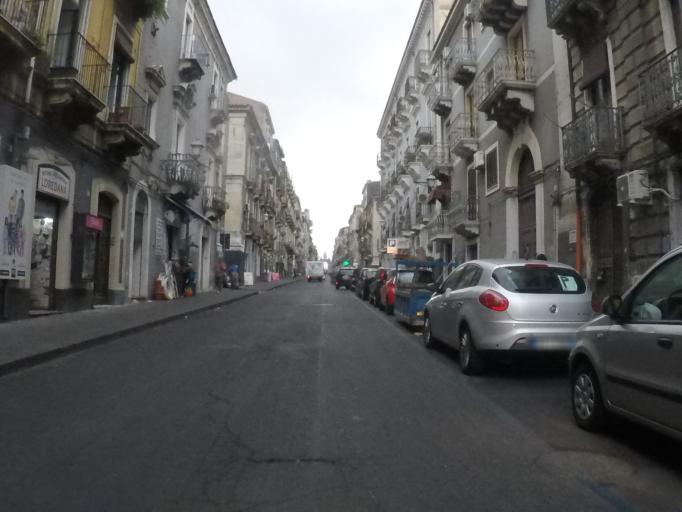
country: IT
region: Sicily
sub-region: Catania
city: Catania
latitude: 37.5010
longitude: 15.0807
